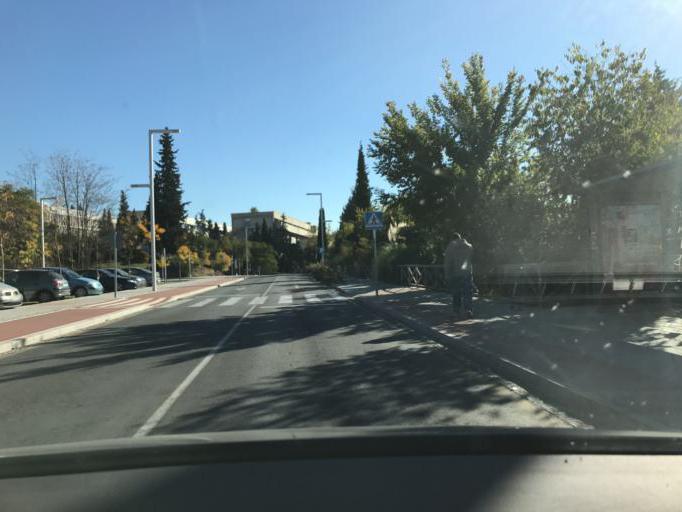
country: ES
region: Andalusia
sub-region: Provincia de Granada
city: Granada
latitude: 37.1943
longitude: -3.5953
